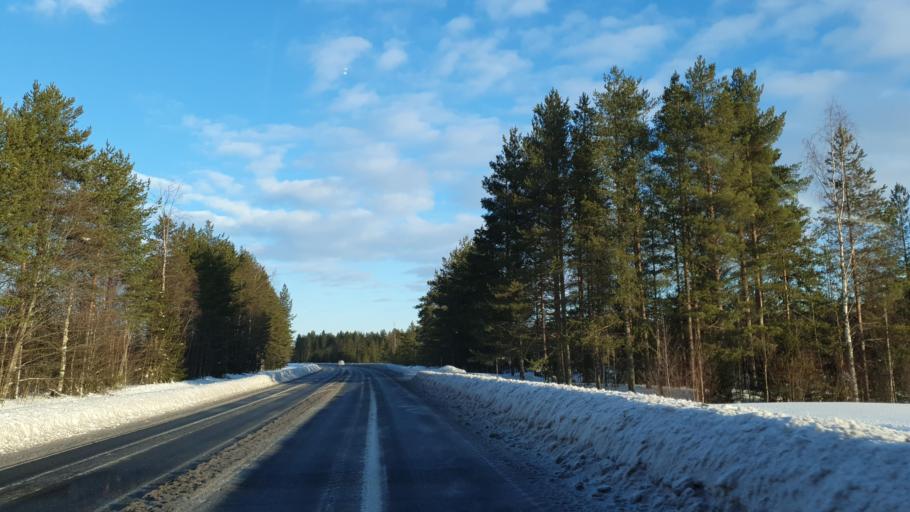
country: FI
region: Northern Ostrobothnia
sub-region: Oulunkaari
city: Utajaervi
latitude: 64.6899
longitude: 26.5392
